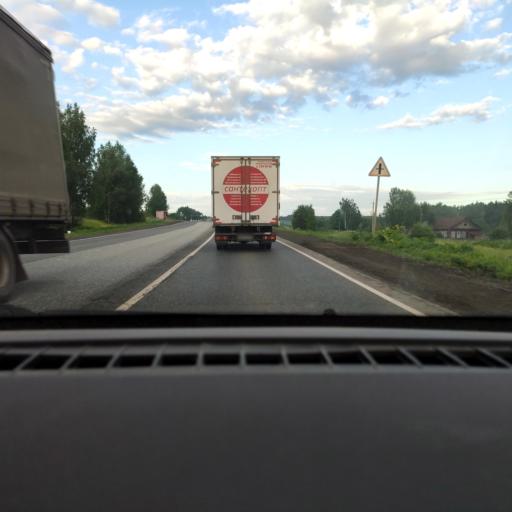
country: RU
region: Perm
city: Nytva
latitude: 57.9423
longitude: 55.1276
